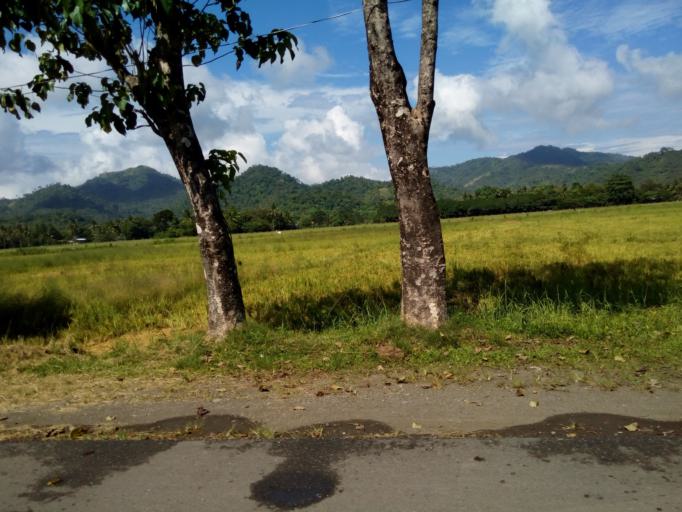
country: PH
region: Caraga
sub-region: Province of Surigao del Norte
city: Luna
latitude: 9.7575
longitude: 125.4827
